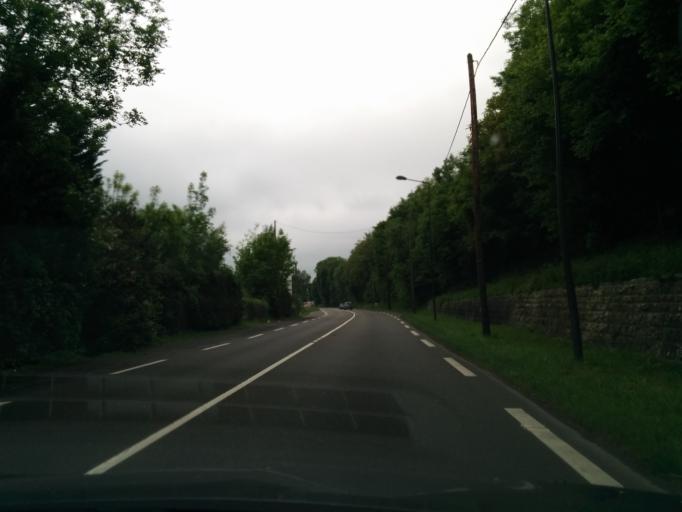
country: FR
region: Ile-de-France
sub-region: Departement des Yvelines
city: Rosny-sur-Seine
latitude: 49.0099
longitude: 1.6141
